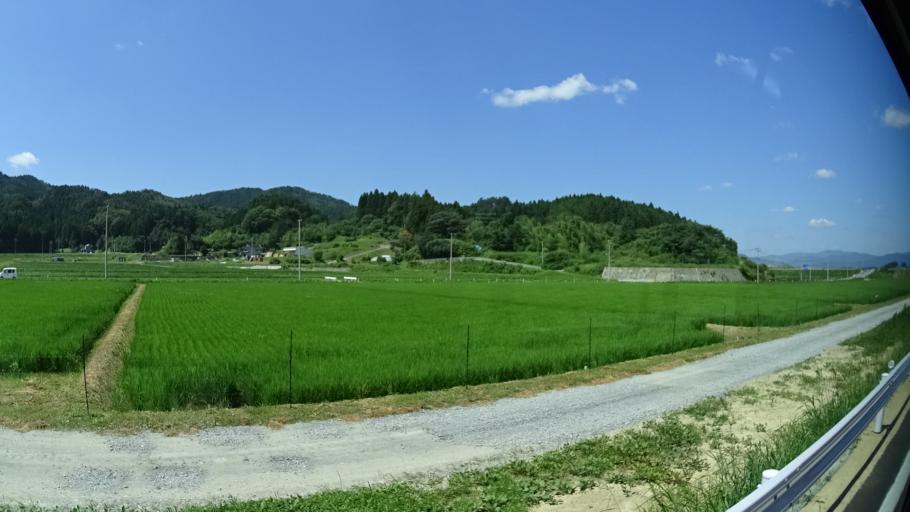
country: JP
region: Iwate
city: Ofunato
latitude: 38.9915
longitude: 141.6962
